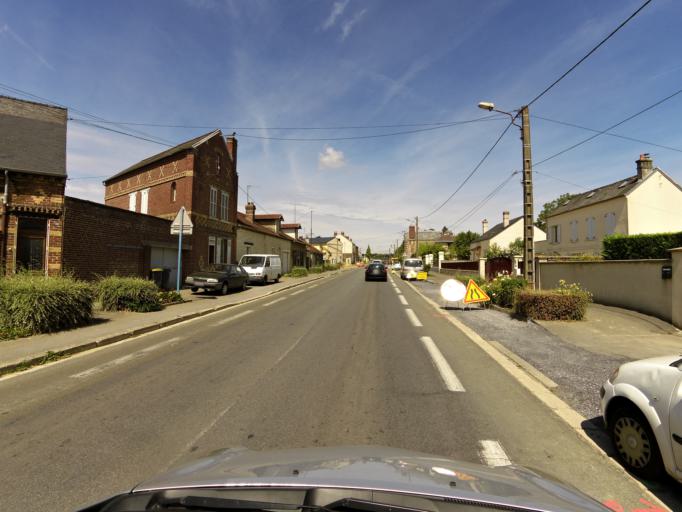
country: FR
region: Picardie
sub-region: Departement de l'Aisne
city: Villers-Cotterets
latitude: 49.2466
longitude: 3.0959
